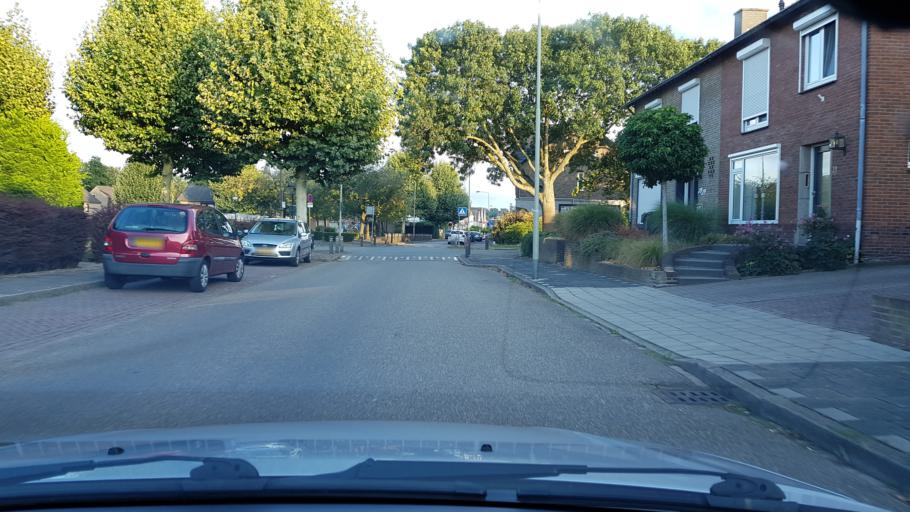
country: NL
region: Limburg
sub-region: Gemeente Sittard-Geleen
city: Limbricht
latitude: 50.9732
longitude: 5.8381
